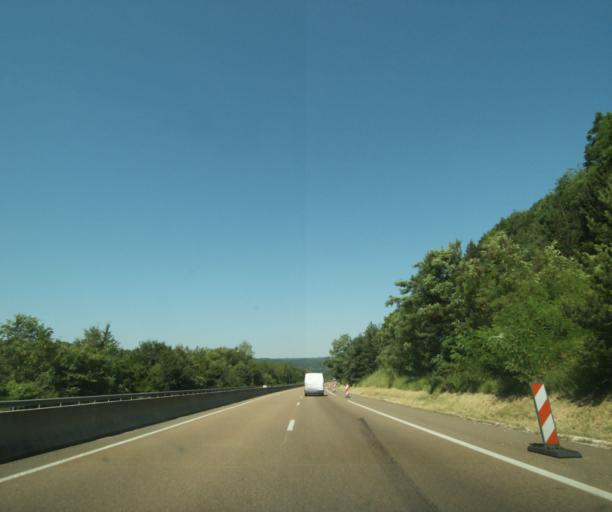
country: FR
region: Lorraine
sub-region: Departement de la Meuse
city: Ligny-en-Barrois
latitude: 48.6927
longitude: 5.3425
